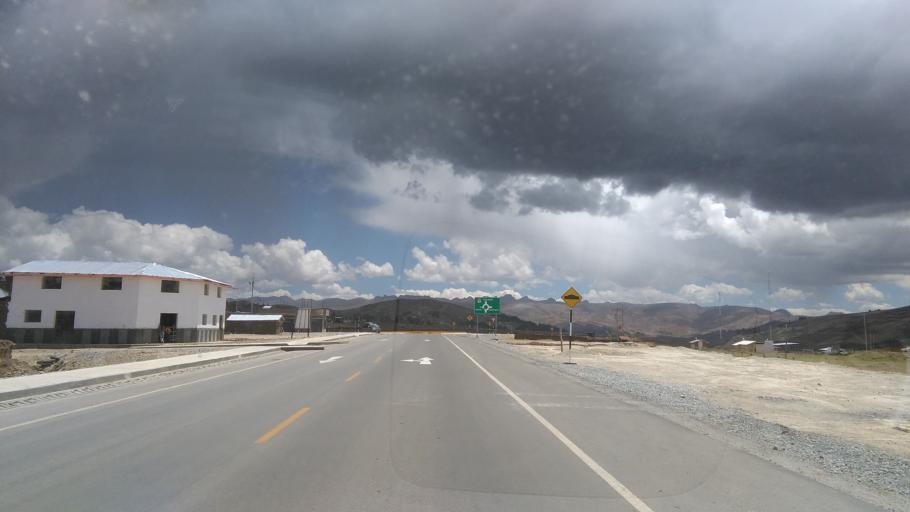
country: PE
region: Apurimac
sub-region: Provincia de Andahuaylas
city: San Jeronimo
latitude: -13.7119
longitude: -73.3497
